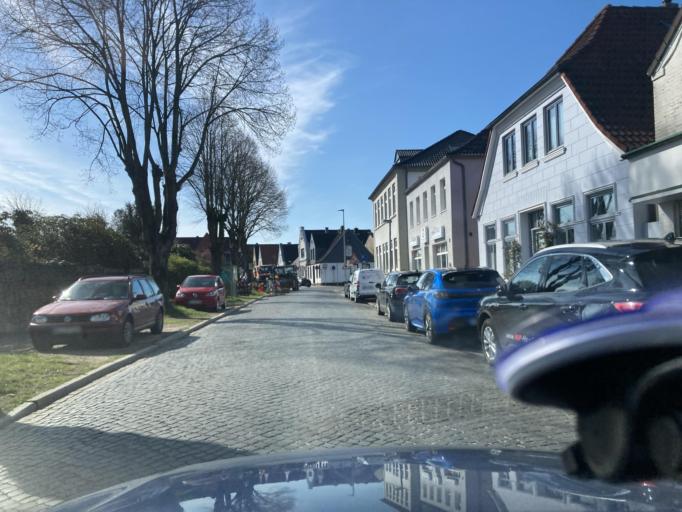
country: DE
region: Schleswig-Holstein
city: Heide
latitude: 54.1992
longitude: 9.0939
